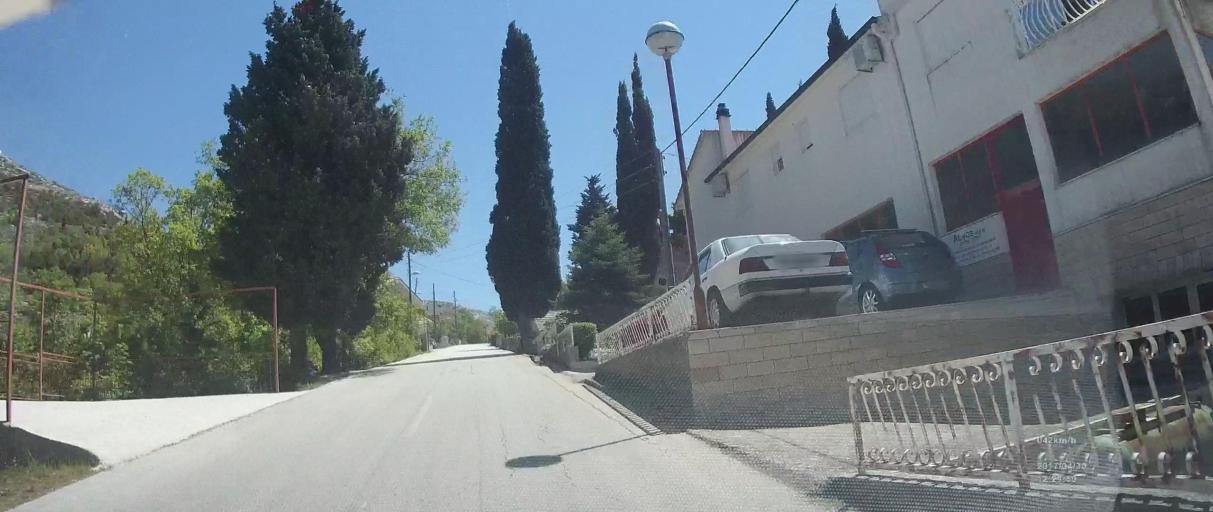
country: HR
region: Splitsko-Dalmatinska
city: Srinjine
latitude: 43.5018
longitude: 16.6016
